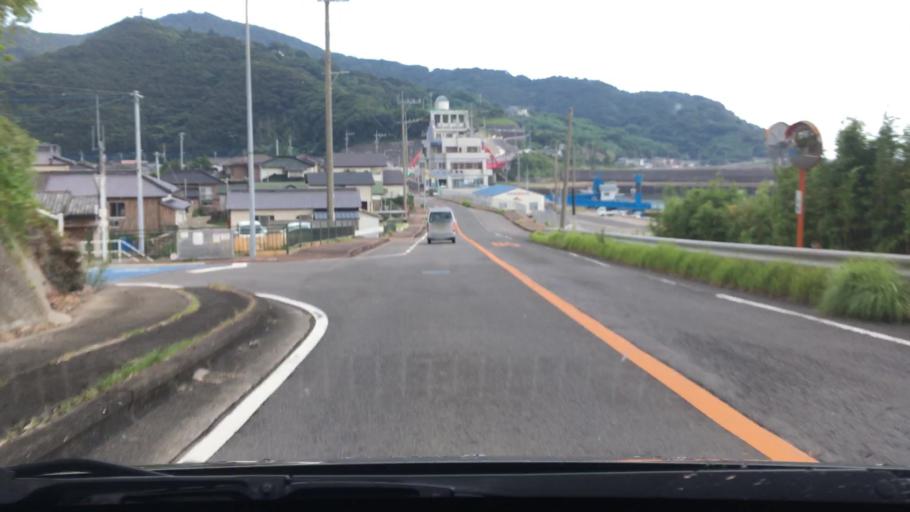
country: JP
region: Nagasaki
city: Togitsu
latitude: 32.8825
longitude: 129.6790
